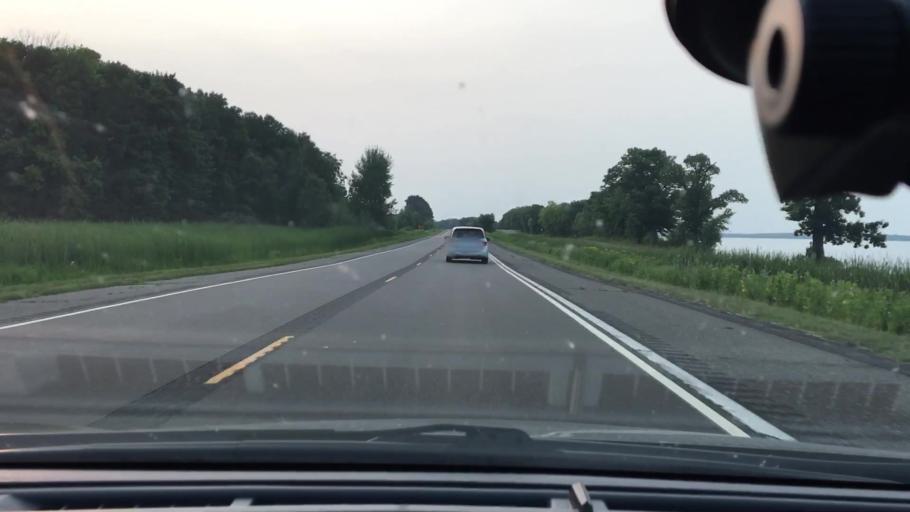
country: US
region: Minnesota
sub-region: Mille Lacs County
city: Vineland
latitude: 46.1359
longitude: -93.6947
